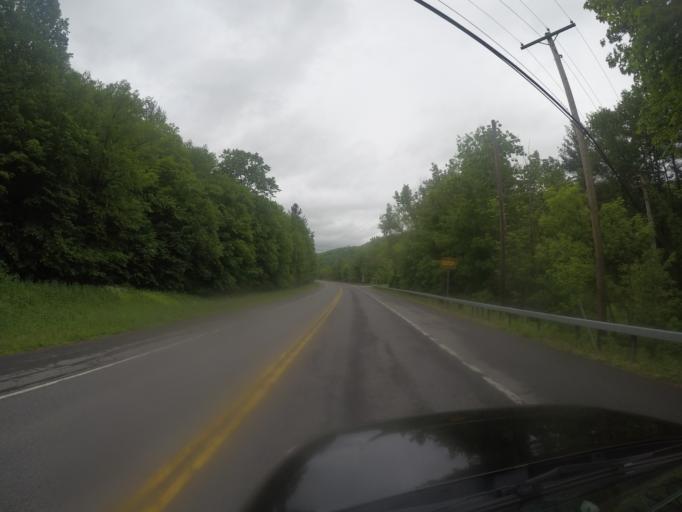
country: US
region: New York
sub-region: Ulster County
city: Shokan
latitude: 42.0755
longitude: -74.3071
